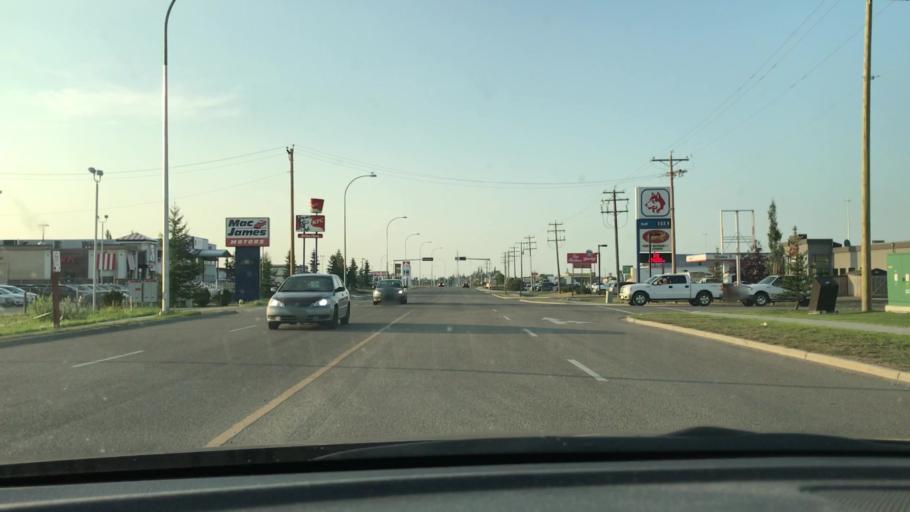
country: CA
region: Alberta
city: Red Deer
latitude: 52.2074
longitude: -113.8160
